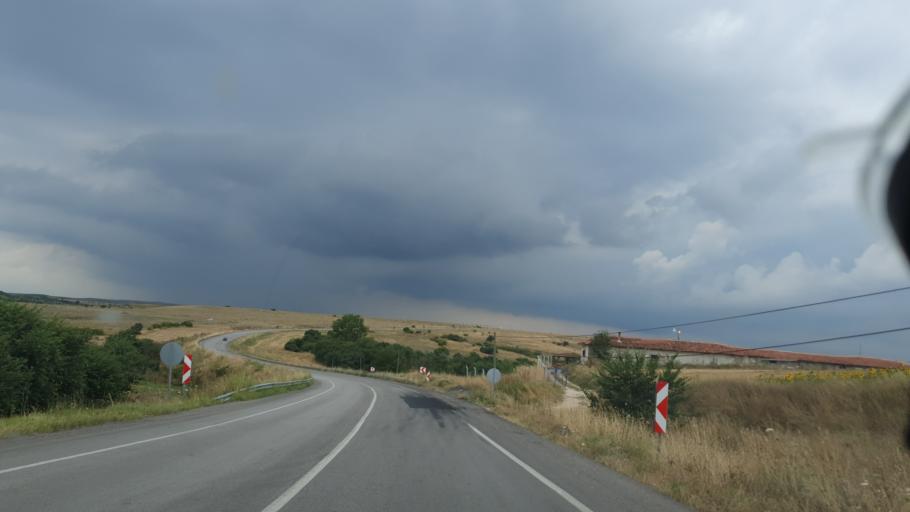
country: TR
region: Tekirdag
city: Hayrabolu
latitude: 41.2201
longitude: 27.0654
